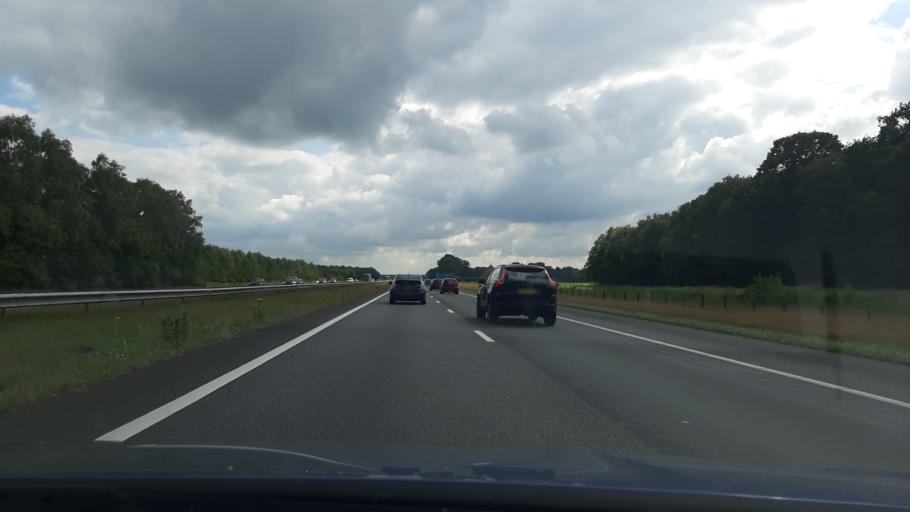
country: NL
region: Friesland
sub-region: Gemeente Smallingerland
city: Boornbergum
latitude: 53.0698
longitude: 6.0596
